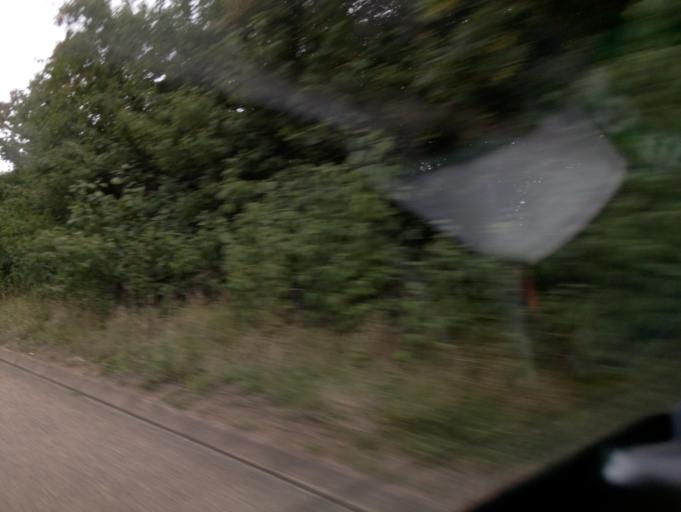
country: GB
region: England
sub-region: Devon
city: Exminster
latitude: 50.6863
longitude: -3.4961
